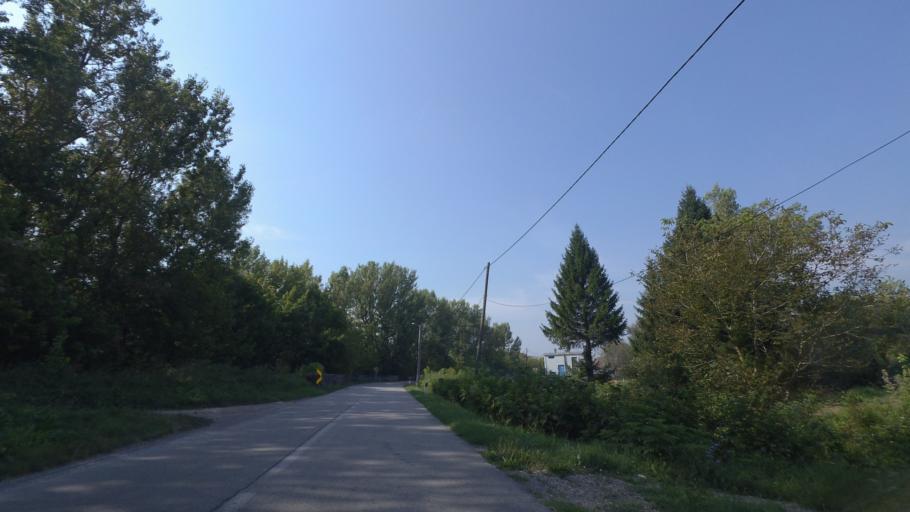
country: BA
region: Republika Srpska
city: Bosanska Dubica
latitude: 45.2474
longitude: 16.8772
